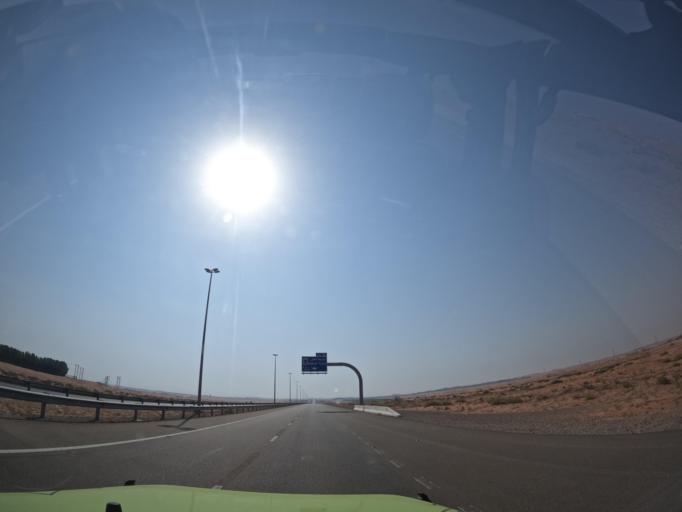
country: OM
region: Al Buraimi
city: Al Buraymi
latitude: 24.4141
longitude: 55.6976
